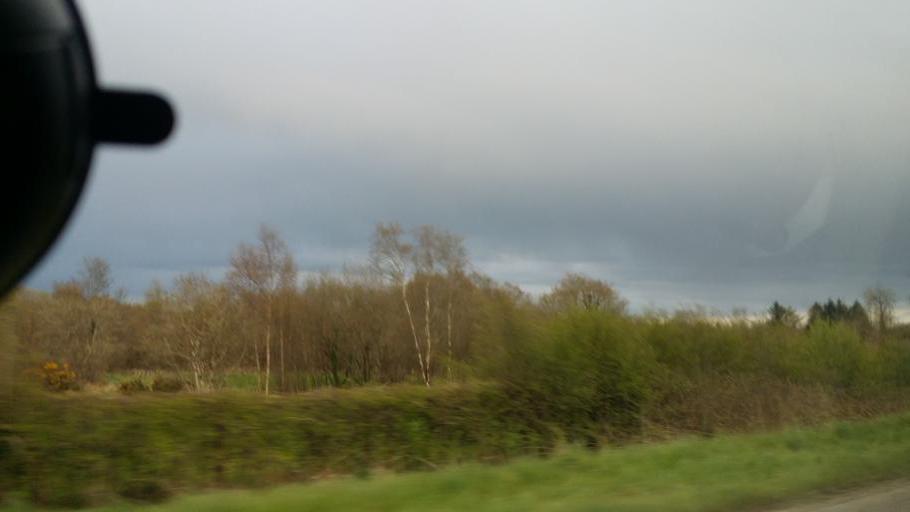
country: IE
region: Ulster
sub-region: An Cabhan
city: Virginia
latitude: 53.8718
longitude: -7.1212
